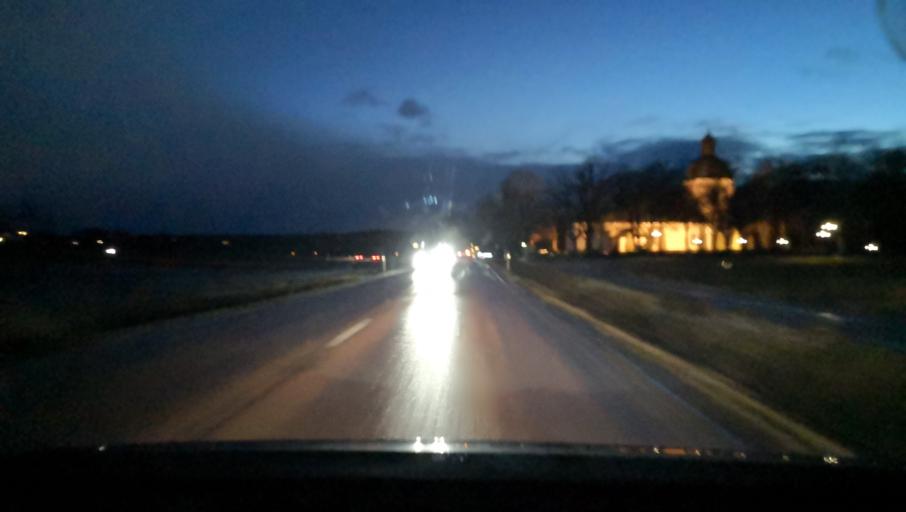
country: SE
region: Vaestmanland
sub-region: Vasteras
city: Skultuna
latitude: 59.7015
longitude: 16.4295
